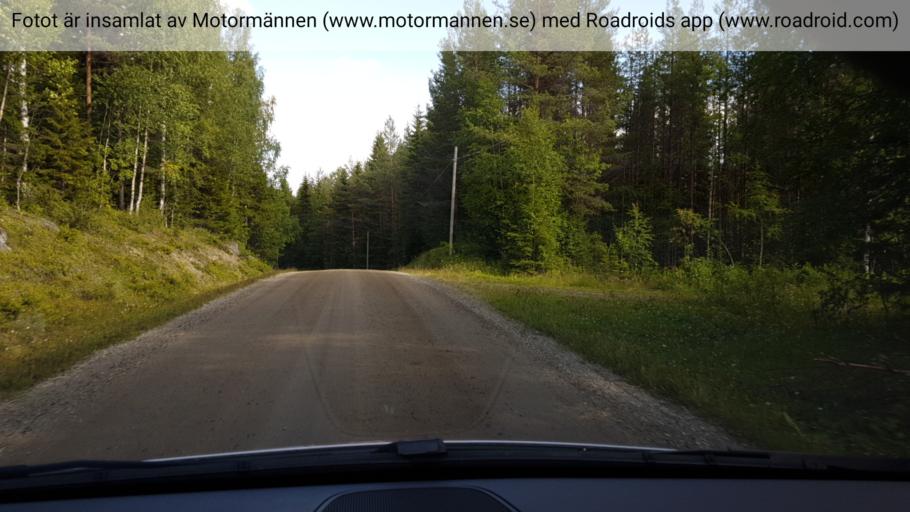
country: SE
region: Jaemtland
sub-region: Ragunda Kommun
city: Hammarstrand
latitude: 63.2834
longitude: 15.9887
